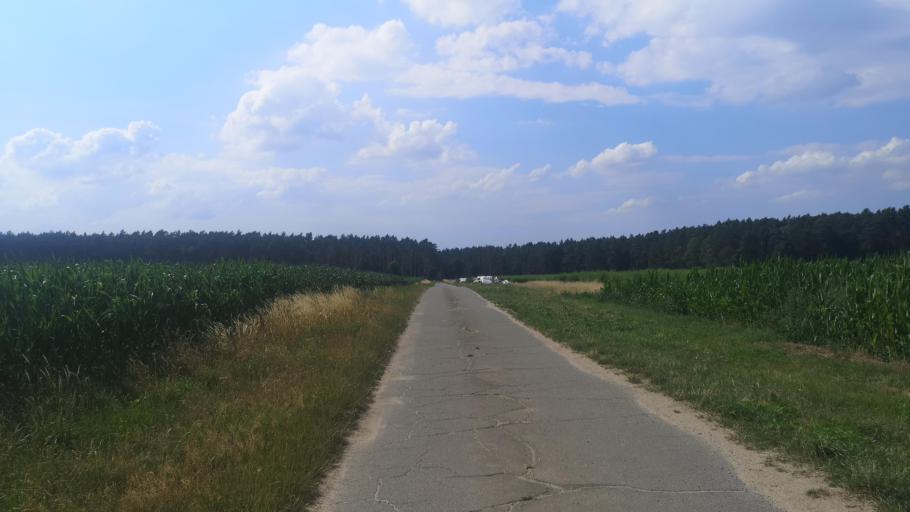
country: DE
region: Lower Saxony
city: Dahlem
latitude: 53.2094
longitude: 10.7446
